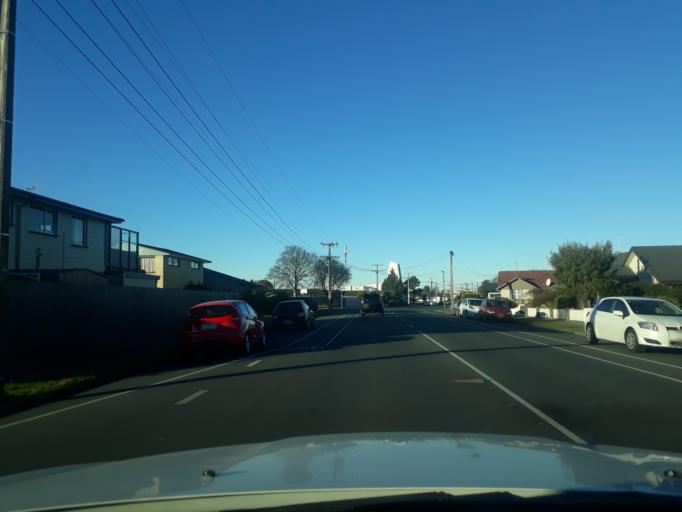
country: NZ
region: Canterbury
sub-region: Timaru District
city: Timaru
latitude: -44.3875
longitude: 171.2002
